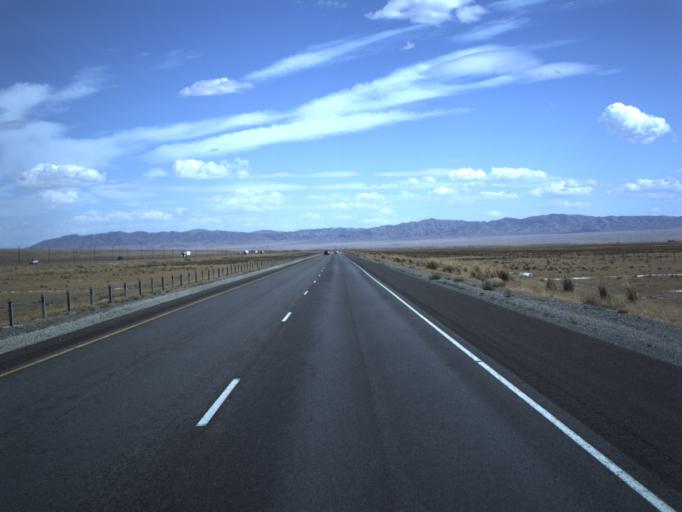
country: US
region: Utah
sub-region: Tooele County
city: Grantsville
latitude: 40.7255
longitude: -113.1833
